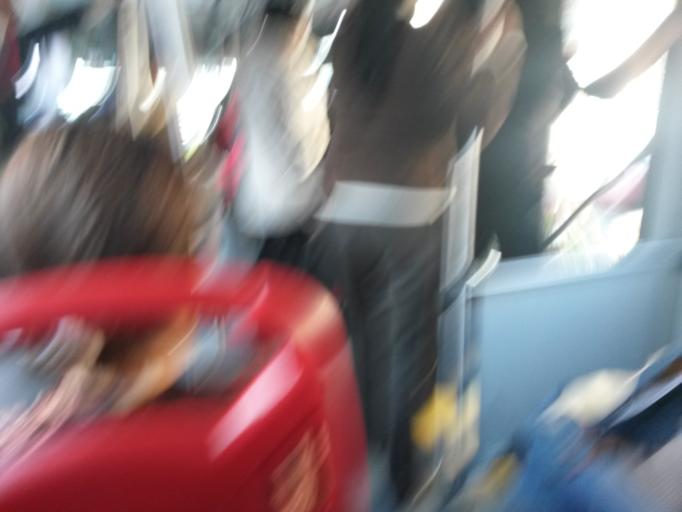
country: EC
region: Pichincha
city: Quito
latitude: -0.1794
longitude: -78.4892
